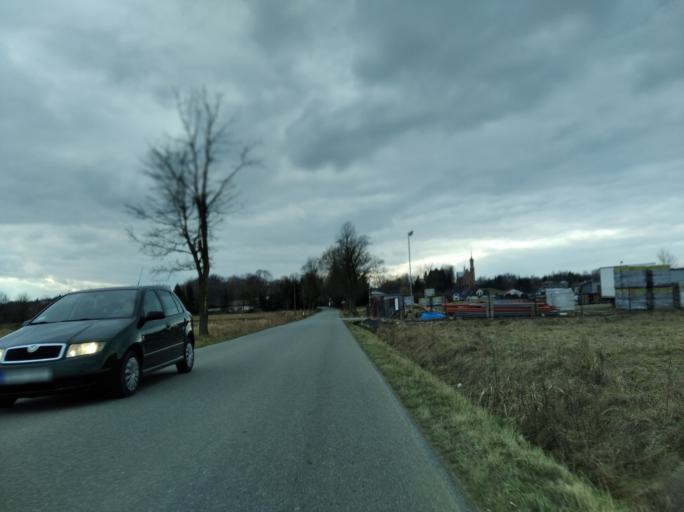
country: PL
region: Subcarpathian Voivodeship
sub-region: Powiat krosnienski
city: Odrzykon
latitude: 49.7501
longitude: 21.7066
